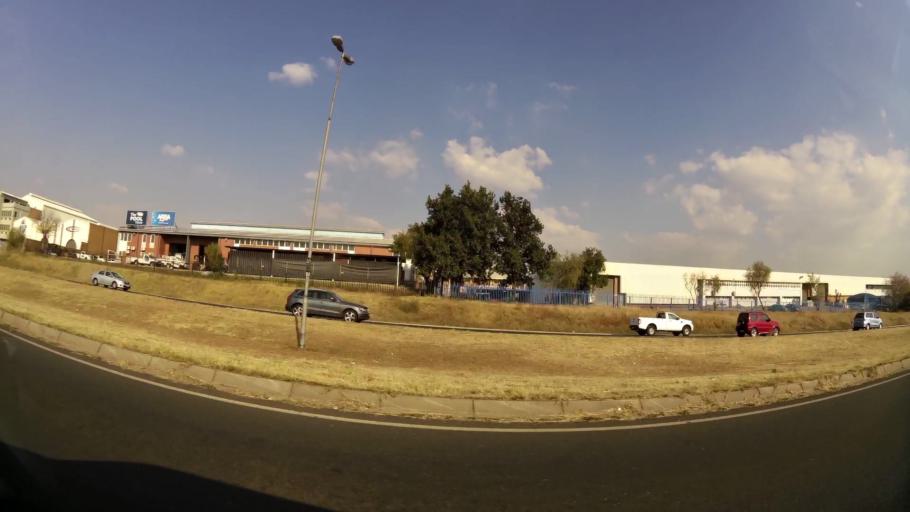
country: ZA
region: Gauteng
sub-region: City of Johannesburg Metropolitan Municipality
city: Modderfontein
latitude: -26.1045
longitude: 28.1731
